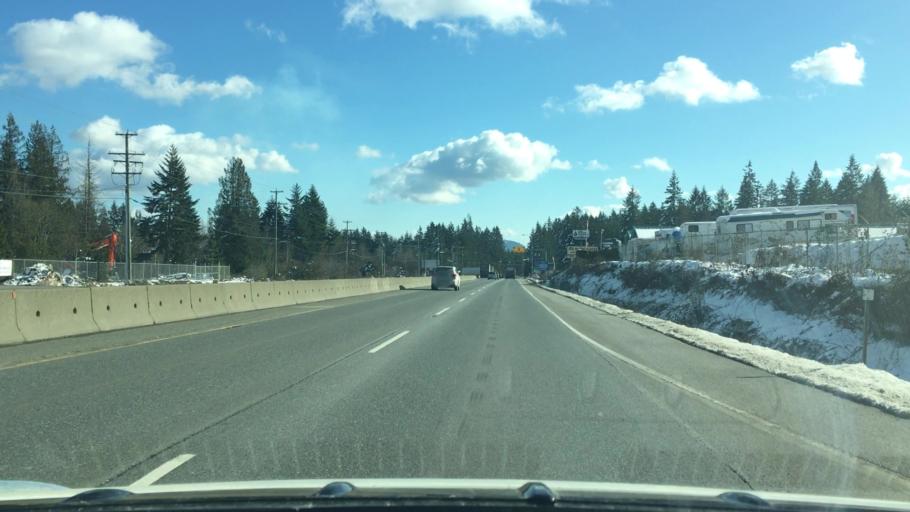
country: CA
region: British Columbia
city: Nanaimo
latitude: 49.0964
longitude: -123.8881
